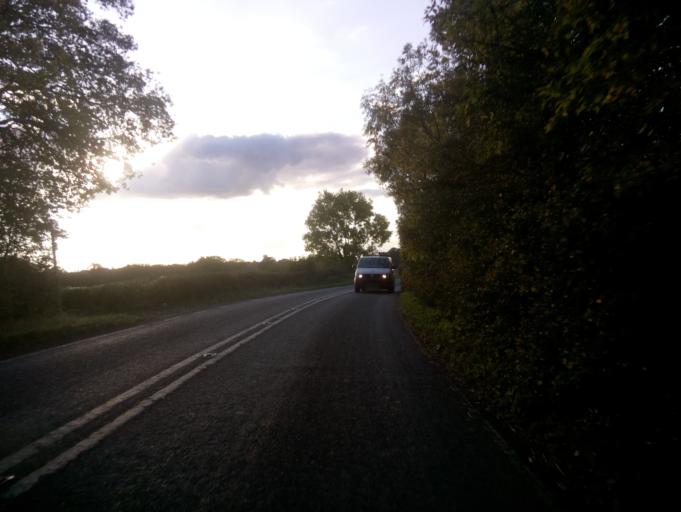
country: GB
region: England
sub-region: Worcestershire
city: Upton upon Severn
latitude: 52.0007
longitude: -2.2535
